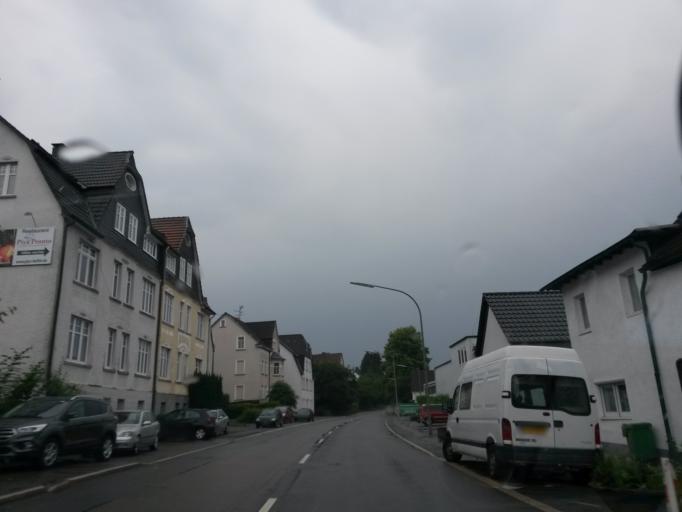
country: DE
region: North Rhine-Westphalia
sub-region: Regierungsbezirk Koln
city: Gummersbach
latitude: 51.0402
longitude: 7.5554
